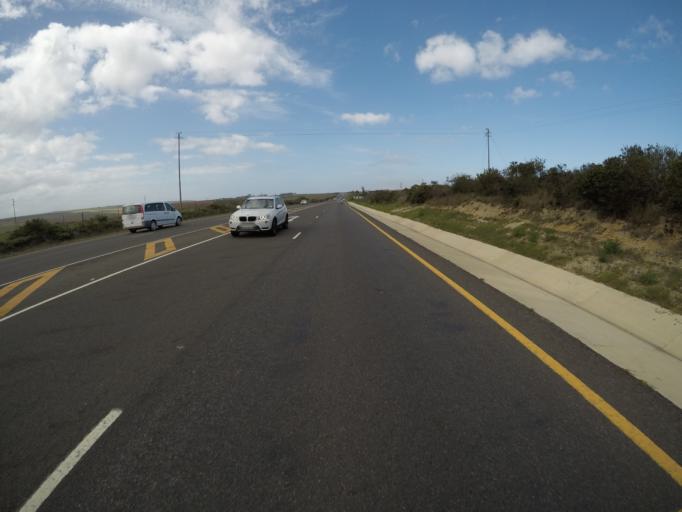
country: ZA
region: Western Cape
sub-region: Eden District Municipality
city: Mossel Bay
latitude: -34.1813
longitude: 22.0304
